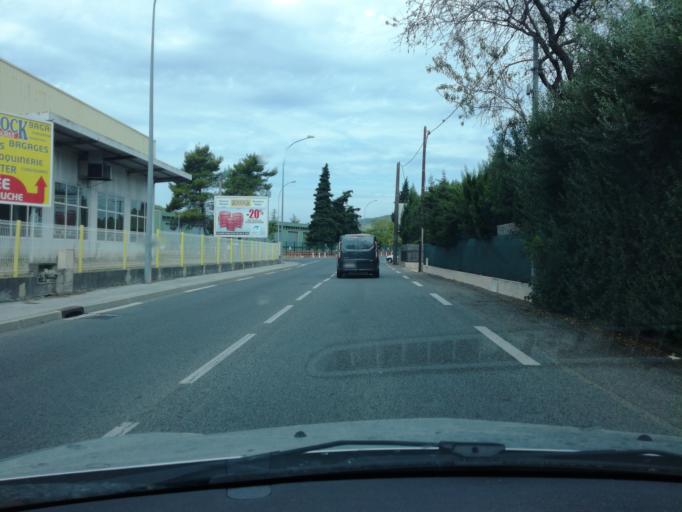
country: FR
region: Provence-Alpes-Cote d'Azur
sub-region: Departement du Var
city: Draguignan
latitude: 43.5233
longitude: 6.4628
